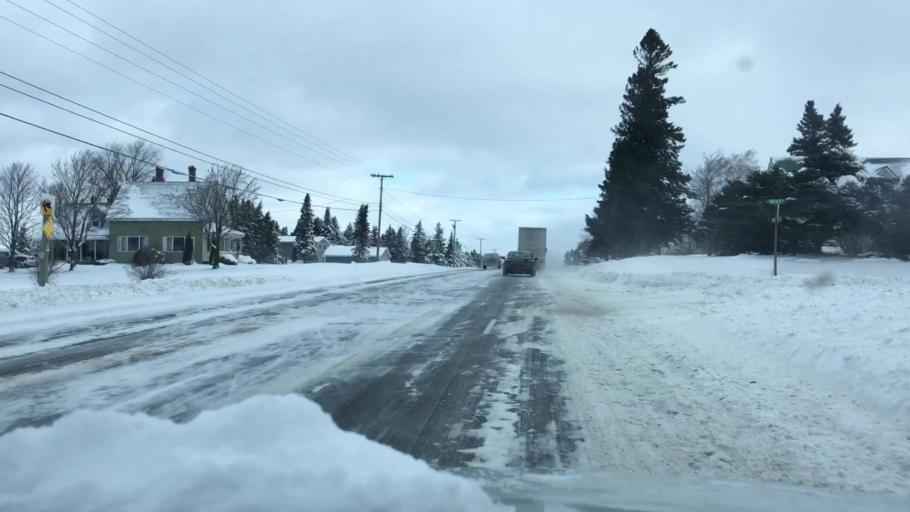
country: US
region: Maine
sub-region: Aroostook County
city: Presque Isle
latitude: 46.7279
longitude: -68.0032
